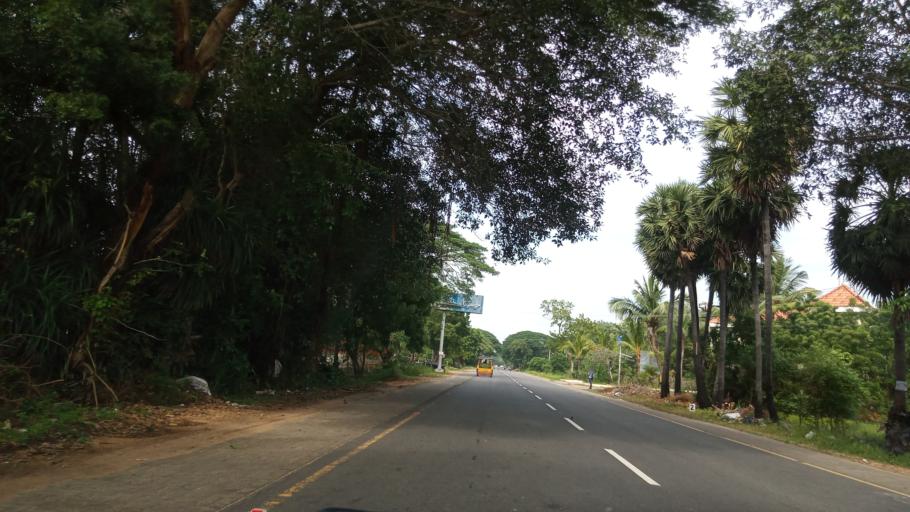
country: IN
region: Tamil Nadu
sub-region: Villupuram
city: Auroville
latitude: 12.0663
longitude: 79.8791
